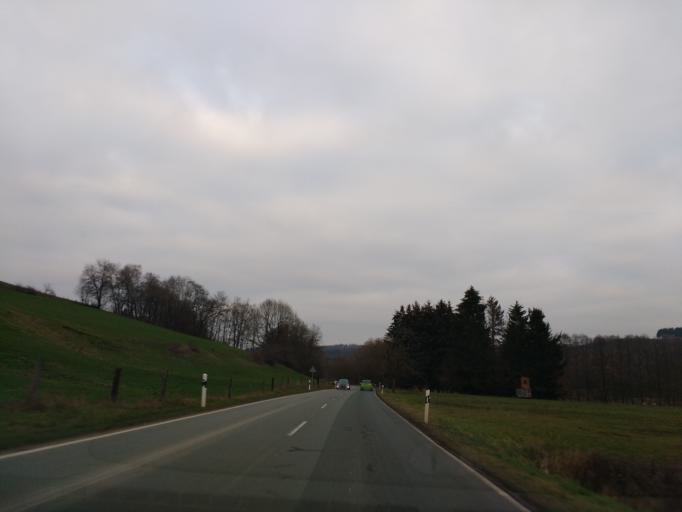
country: DE
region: Hesse
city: Bebra
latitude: 51.0116
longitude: 9.7716
